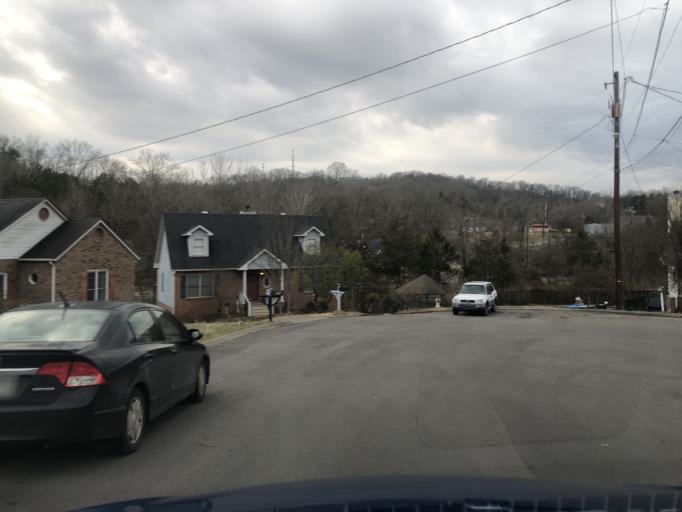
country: US
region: Tennessee
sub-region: Davidson County
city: Belle Meade
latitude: 36.1017
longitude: -86.9299
